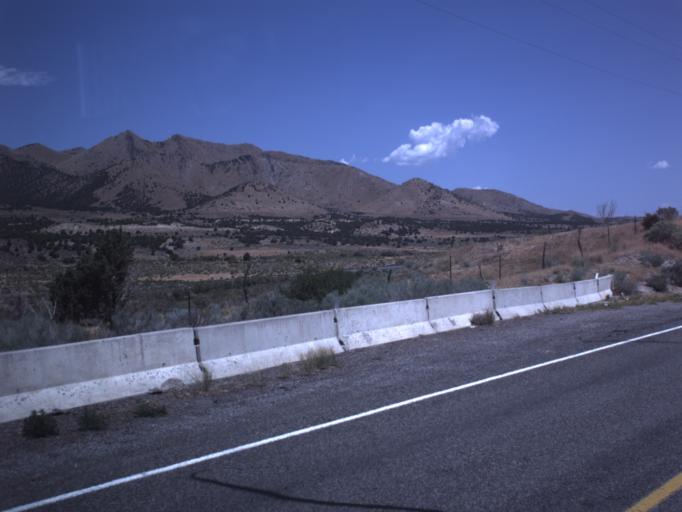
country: US
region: Utah
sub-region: Millard County
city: Delta
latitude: 39.5508
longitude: -112.2233
